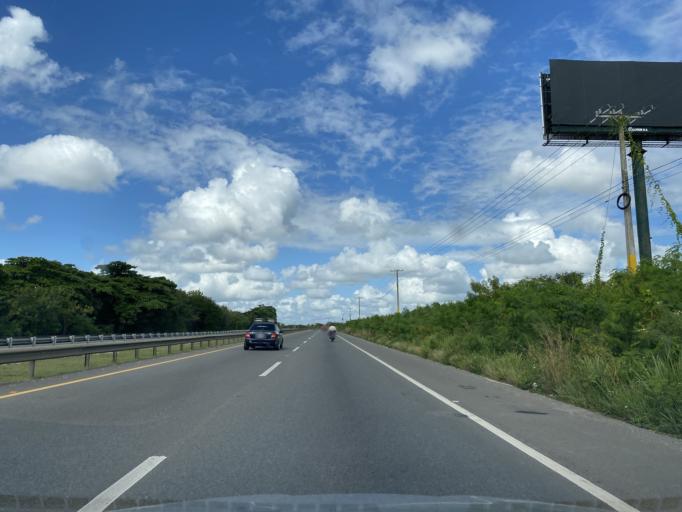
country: DO
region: Santo Domingo
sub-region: Santo Domingo
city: Boca Chica
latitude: 18.4401
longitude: -69.5799
